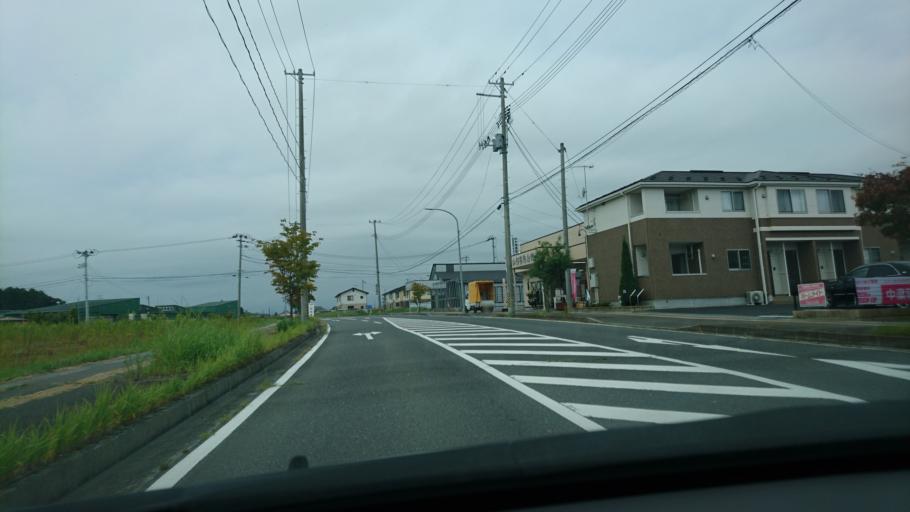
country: JP
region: Iwate
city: Ichinoseki
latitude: 38.7721
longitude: 141.1189
